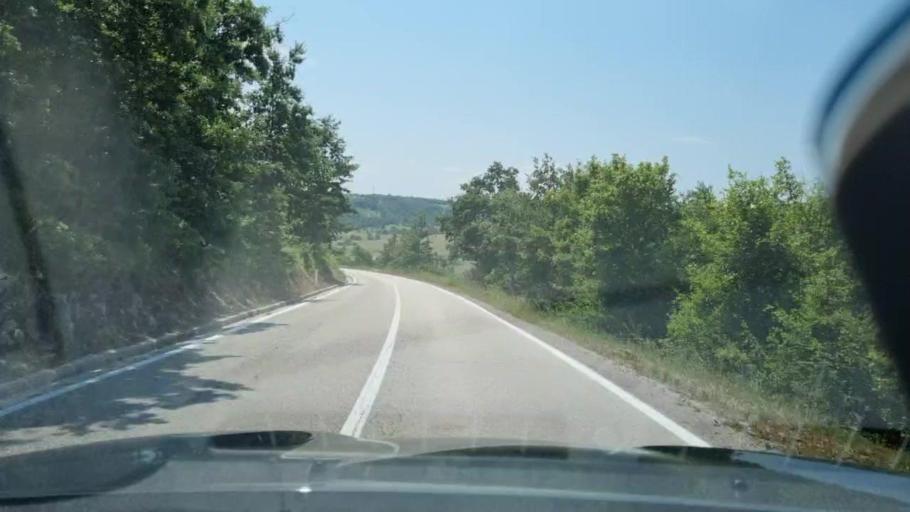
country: BA
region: Federation of Bosnia and Herzegovina
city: Bosansko Grahovo
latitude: 44.4330
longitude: 16.4001
